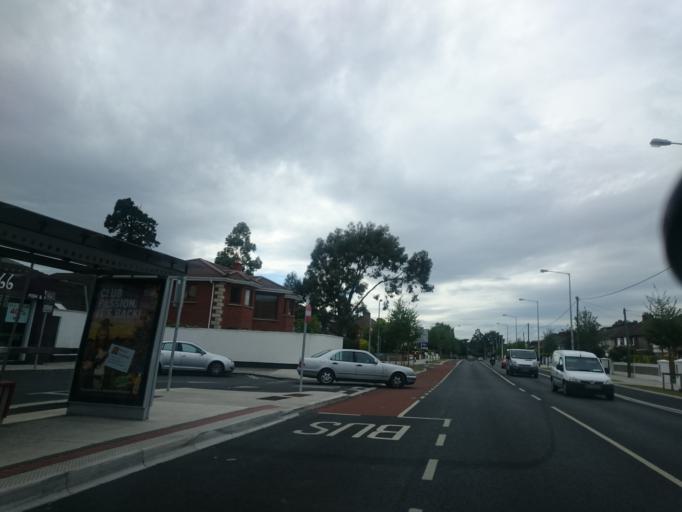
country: IE
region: Leinster
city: Dundrum
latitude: 53.3009
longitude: -6.2635
